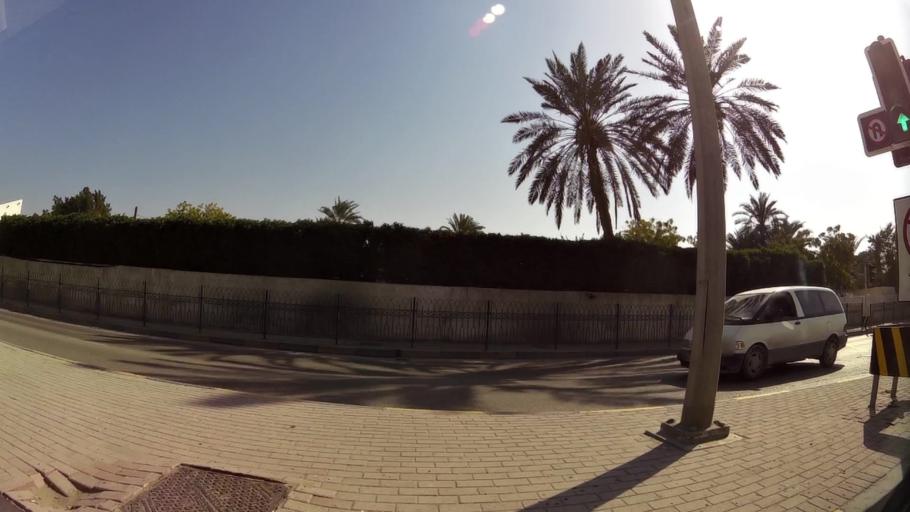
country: BH
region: Manama
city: Manama
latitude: 26.2142
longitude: 50.5818
